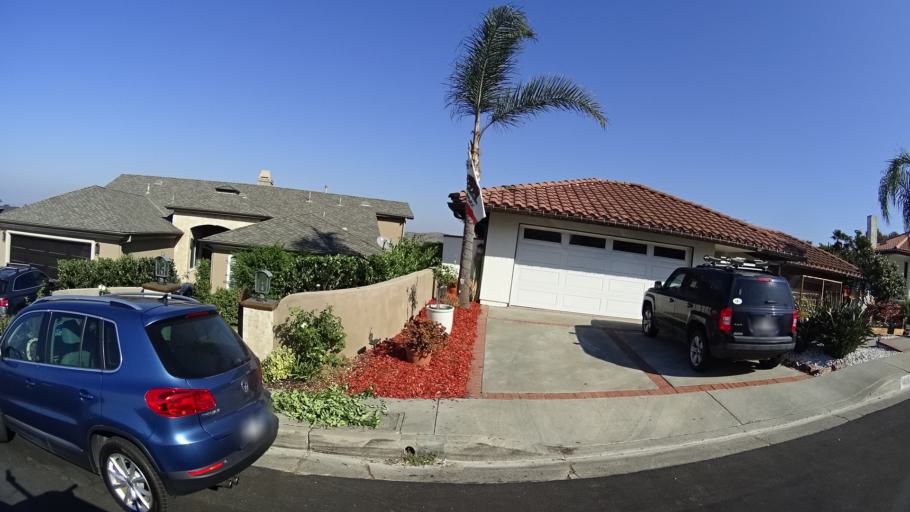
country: US
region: California
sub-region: Orange County
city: San Clemente
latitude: 33.4393
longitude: -117.6078
